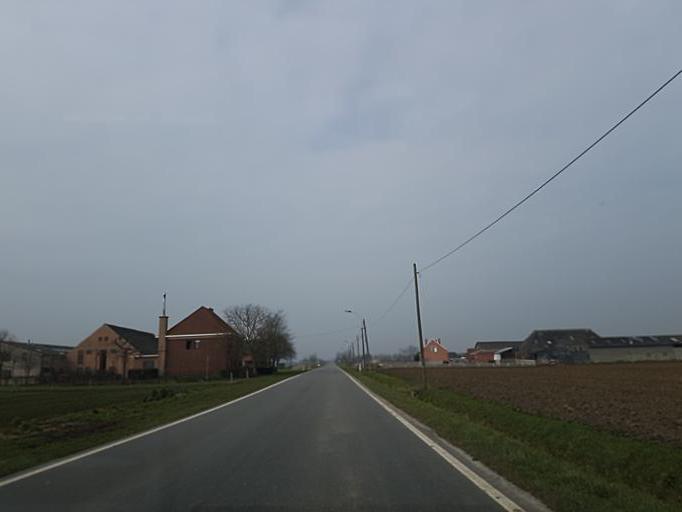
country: BE
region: Flanders
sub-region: Provincie Oost-Vlaanderen
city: Beveren
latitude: 51.3036
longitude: 4.2084
